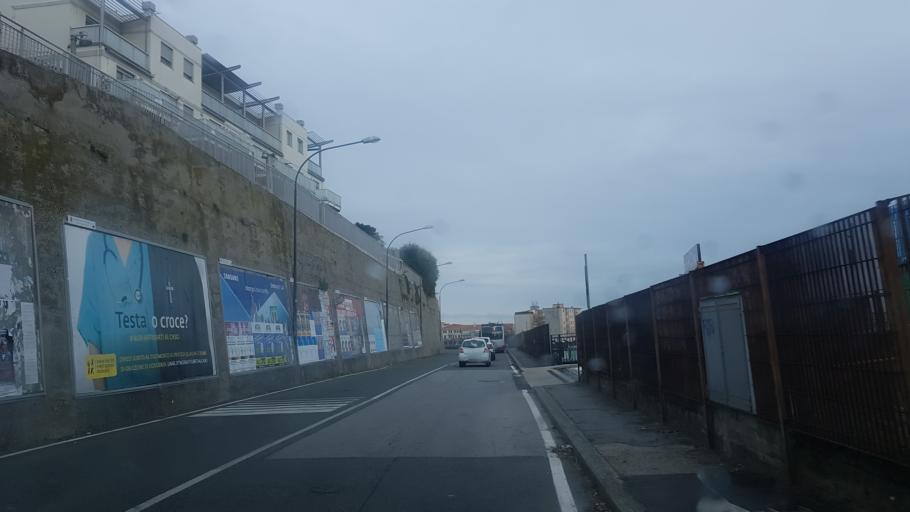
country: IT
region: Liguria
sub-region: Provincia di Savona
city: Savona
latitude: 44.3011
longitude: 8.4628
